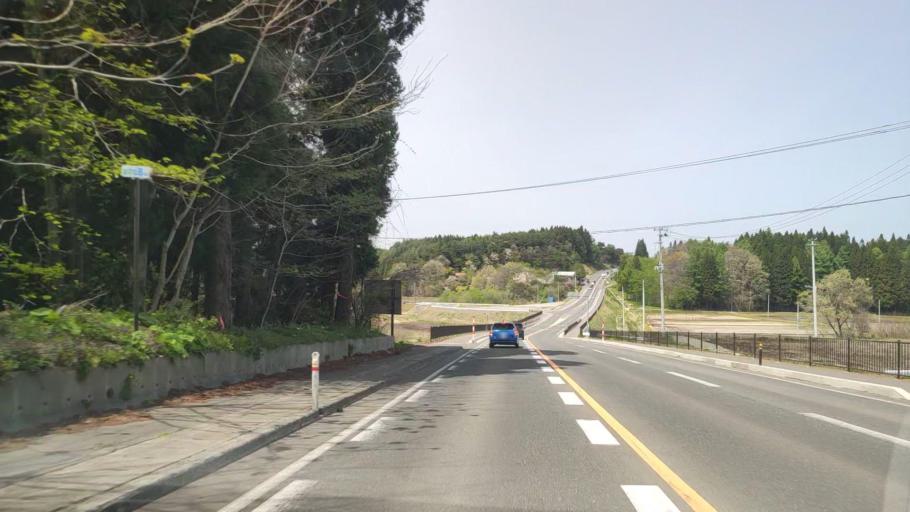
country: JP
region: Aomori
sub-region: Misawa Shi
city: Inuotose
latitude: 40.6624
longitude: 141.1886
